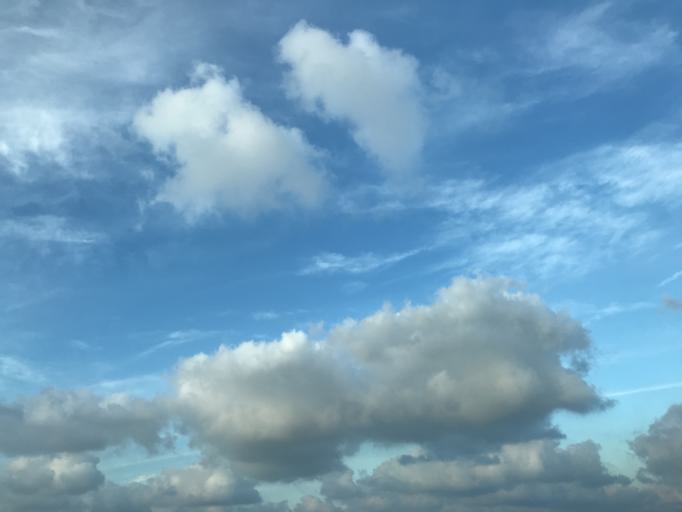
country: TR
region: Istanbul
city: Durusu
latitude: 41.2606
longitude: 28.7133
